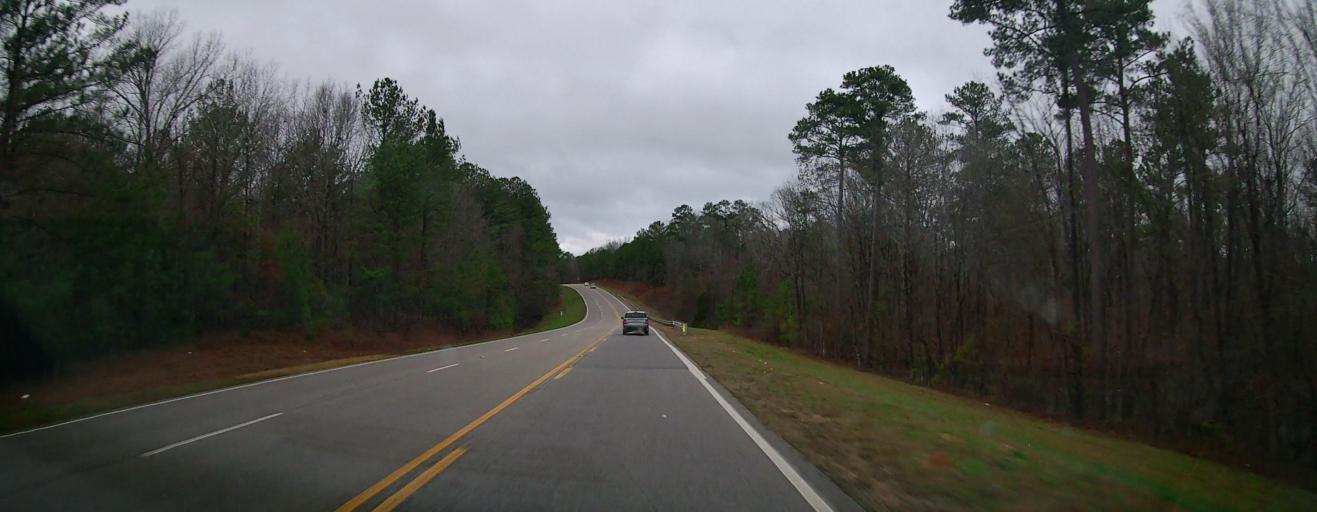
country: US
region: Alabama
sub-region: Bibb County
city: Centreville
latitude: 32.8986
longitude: -86.9938
